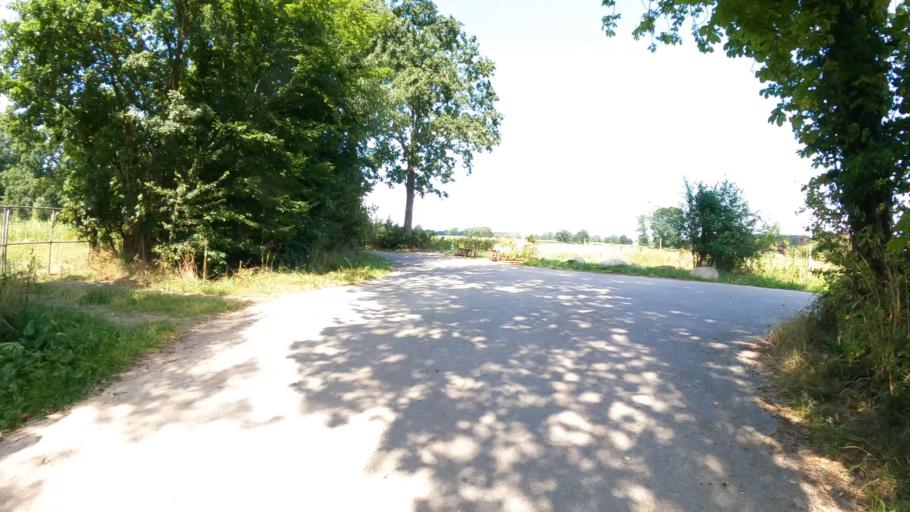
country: DE
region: Schleswig-Holstein
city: Ellerhoop
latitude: 53.7365
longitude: 9.7648
